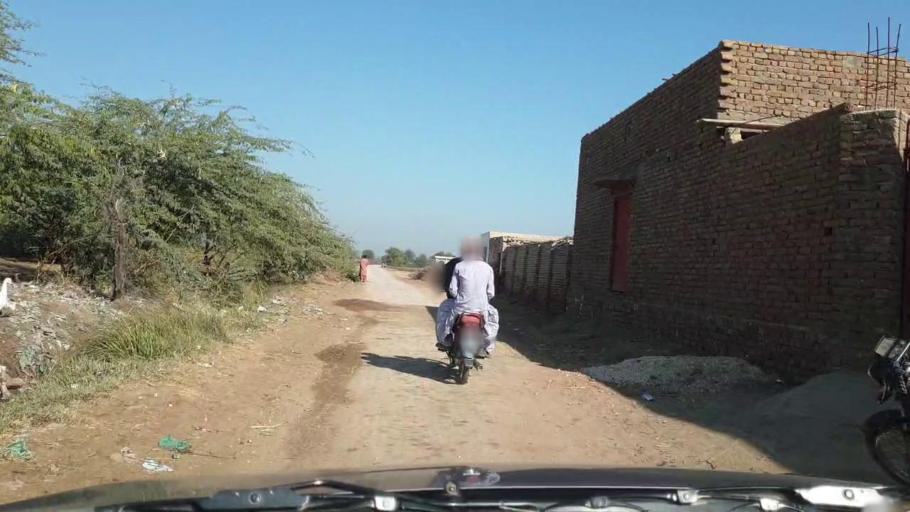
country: PK
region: Sindh
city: Jhol
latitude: 25.9438
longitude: 68.8192
